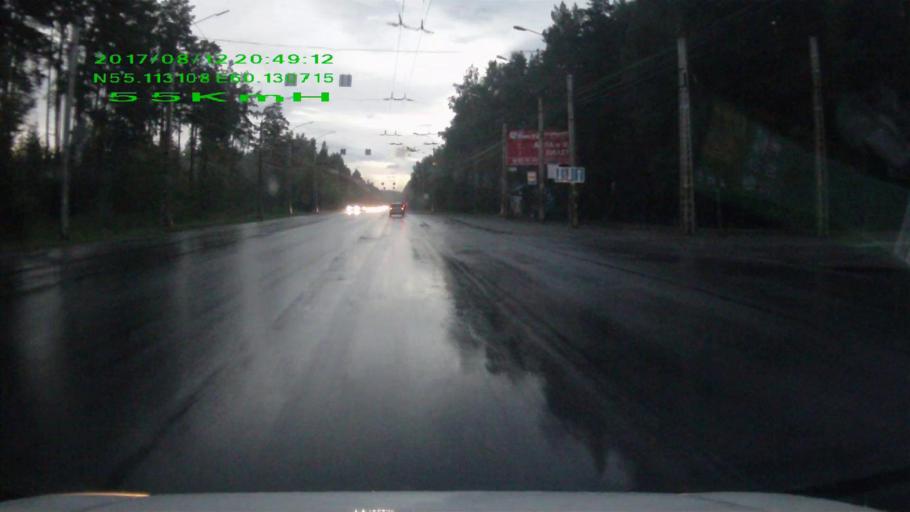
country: RU
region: Chelyabinsk
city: Turgoyak
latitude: 55.1135
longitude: 60.1307
